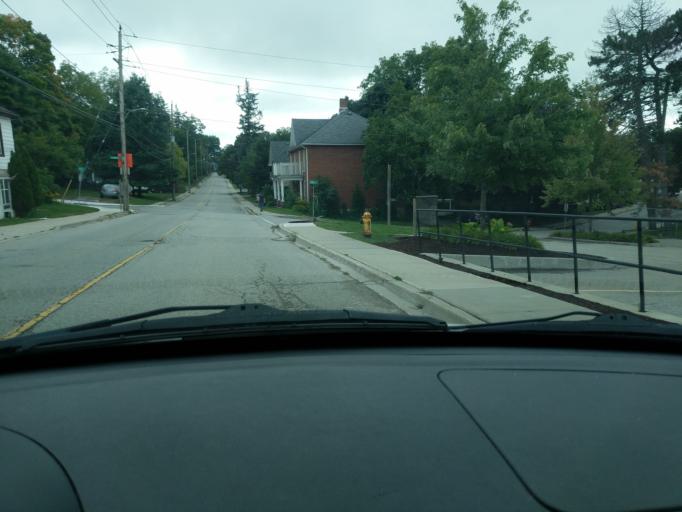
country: CA
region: Ontario
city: Cambridge
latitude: 43.4319
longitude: -80.3069
